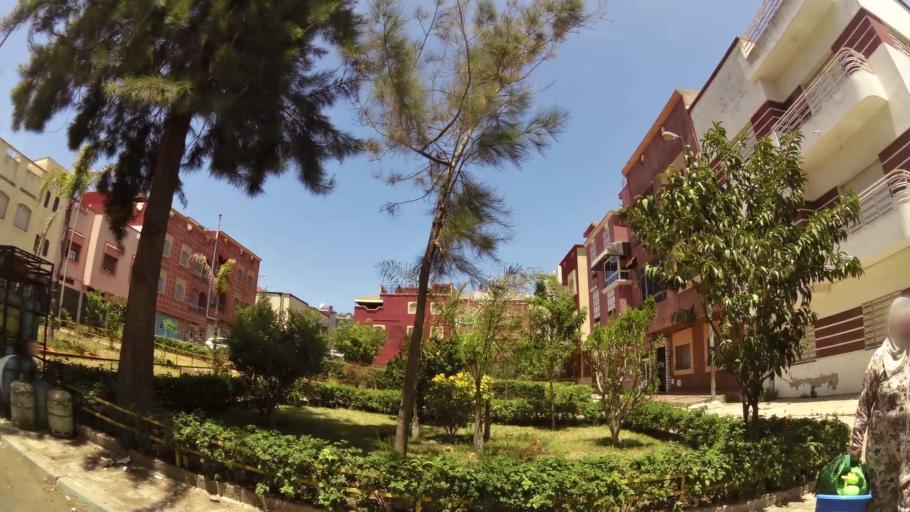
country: MA
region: Gharb-Chrarda-Beni Hssen
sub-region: Kenitra Province
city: Kenitra
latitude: 34.2537
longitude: -6.6177
